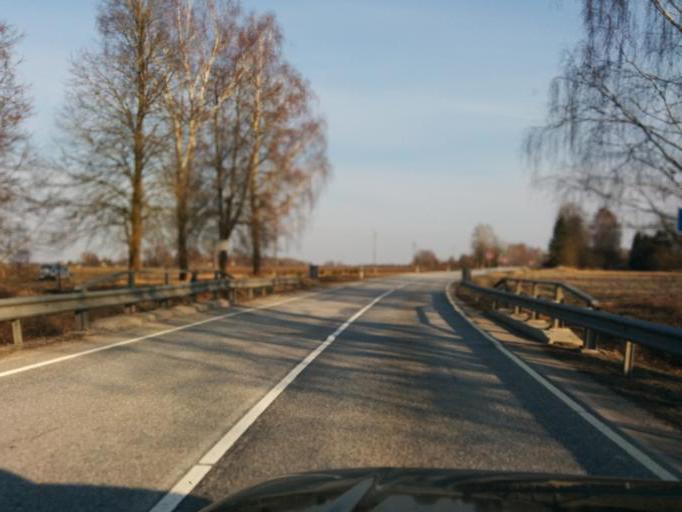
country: LV
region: Lecava
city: Iecava
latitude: 56.5956
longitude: 24.1239
